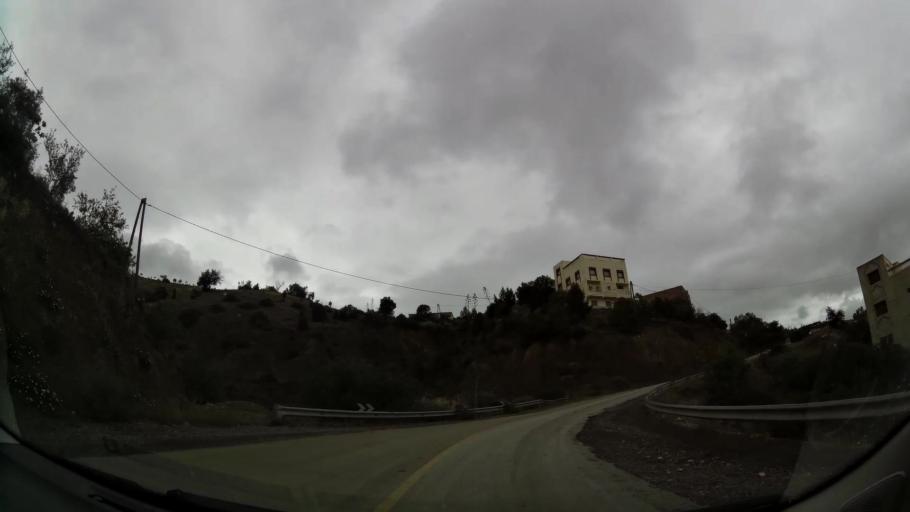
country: MA
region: Taza-Al Hoceima-Taounate
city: Imzourene
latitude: 34.9551
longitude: -3.8090
